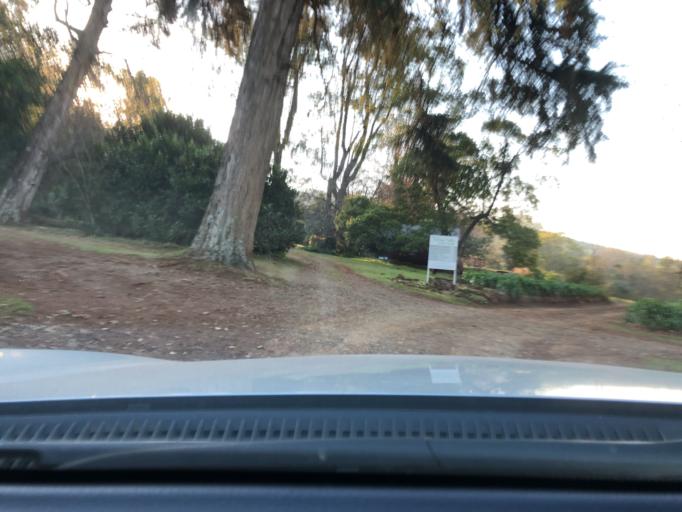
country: ZA
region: KwaZulu-Natal
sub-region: Sisonke District Municipality
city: Ixopo
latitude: -30.1816
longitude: 30.0458
